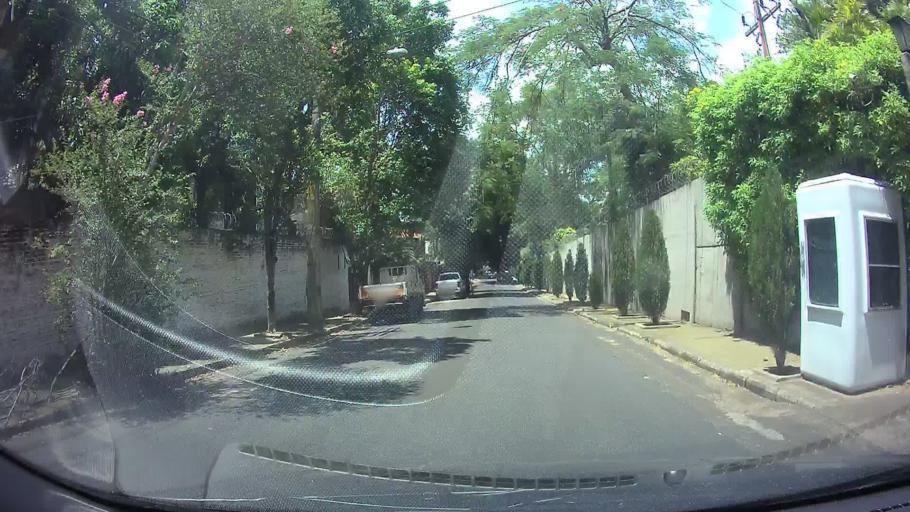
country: PY
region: Asuncion
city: Asuncion
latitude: -25.2961
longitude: -57.6062
